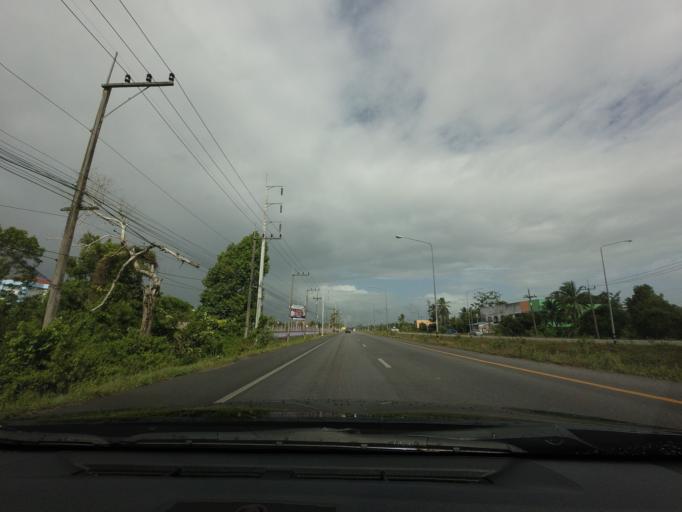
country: TH
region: Pattani
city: Nong Chik
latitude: 6.8075
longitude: 101.1202
